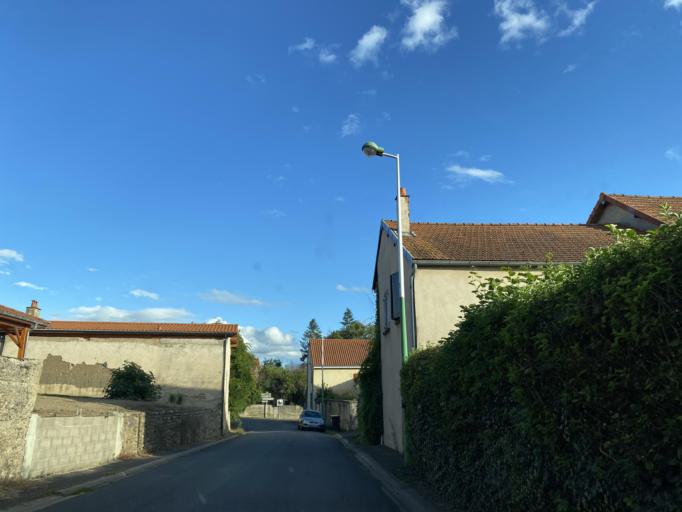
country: FR
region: Auvergne
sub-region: Departement du Puy-de-Dome
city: Puy-Guillaume
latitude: 45.9734
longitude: 3.4446
